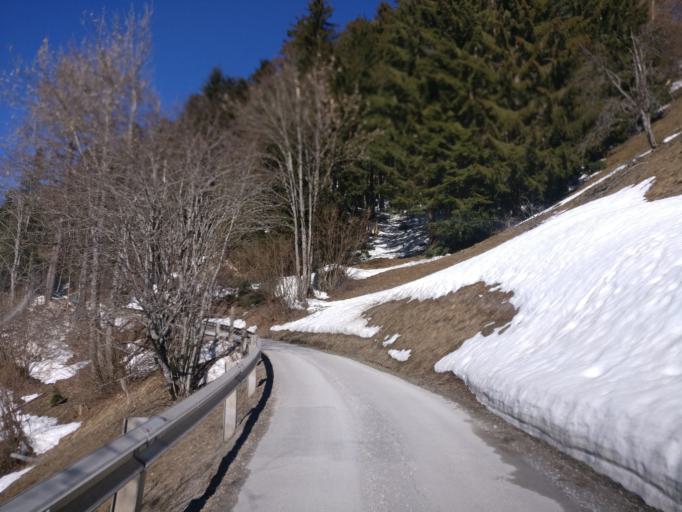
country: AT
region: Salzburg
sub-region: Politischer Bezirk Sankt Johann im Pongau
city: Sankt Johann im Pongau
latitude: 47.3364
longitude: 13.2324
